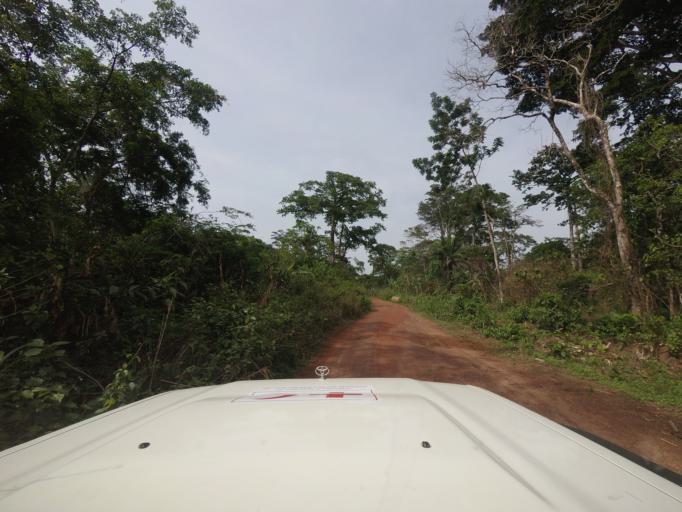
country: GN
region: Nzerekore
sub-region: Macenta
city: Macenta
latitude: 8.5003
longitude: -9.5322
